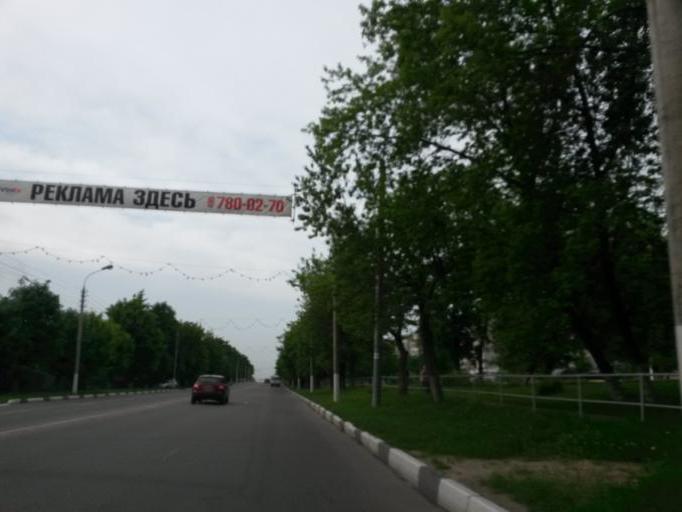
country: RU
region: Moskovskaya
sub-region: Chekhovskiy Rayon
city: Chekhov
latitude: 55.1458
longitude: 37.4546
